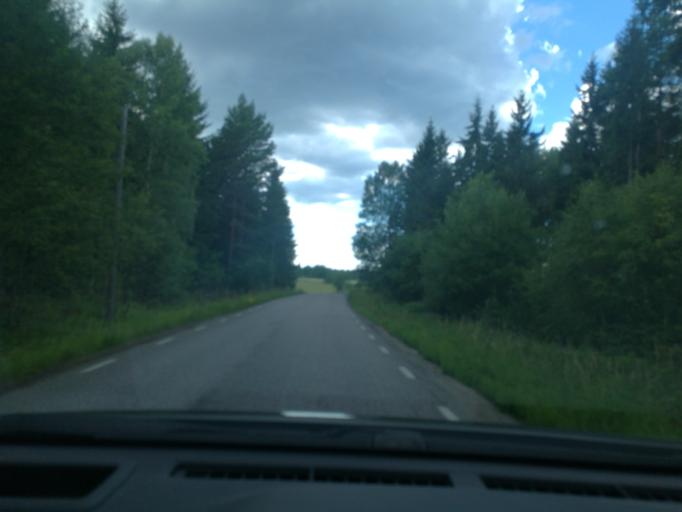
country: SE
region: Soedermanland
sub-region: Eskilstuna Kommun
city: Arla
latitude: 59.4344
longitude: 16.8106
